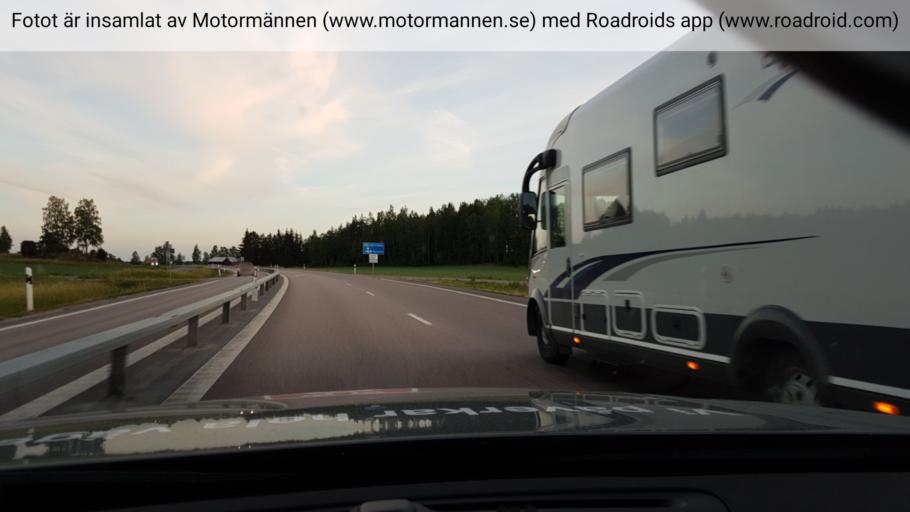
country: SE
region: Vaestmanland
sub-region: Sala Kommun
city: Sala
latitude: 59.8813
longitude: 16.5479
